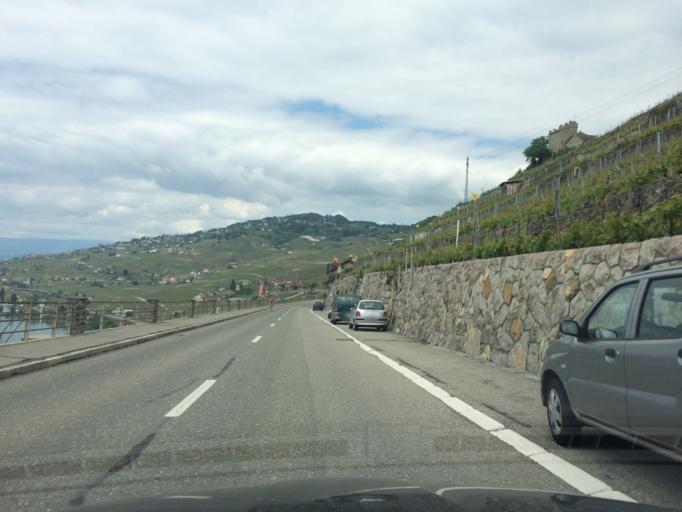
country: CH
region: Vaud
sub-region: Lavaux-Oron District
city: Chexbres
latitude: 46.4859
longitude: 6.7570
